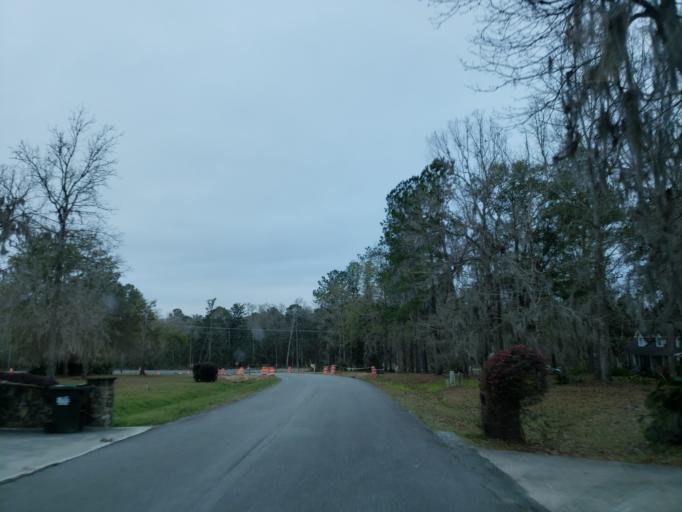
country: US
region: Georgia
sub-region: Lowndes County
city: Remerton
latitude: 30.8952
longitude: -83.3640
